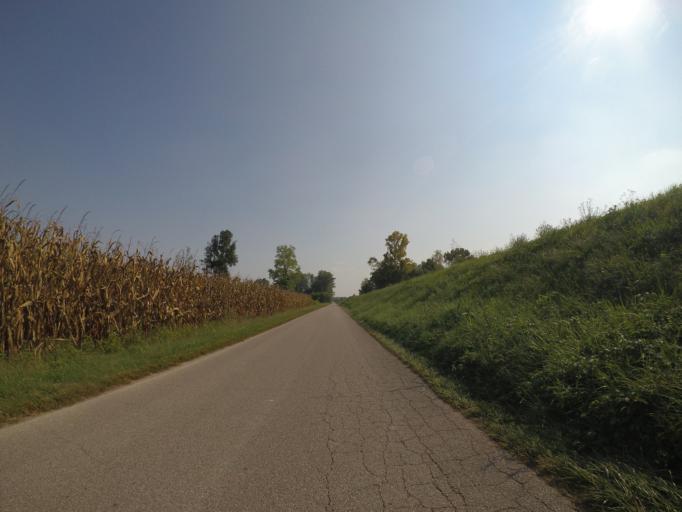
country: IT
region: Friuli Venezia Giulia
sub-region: Provincia di Udine
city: Camino al Tagliamento
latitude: 45.9049
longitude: 12.9358
